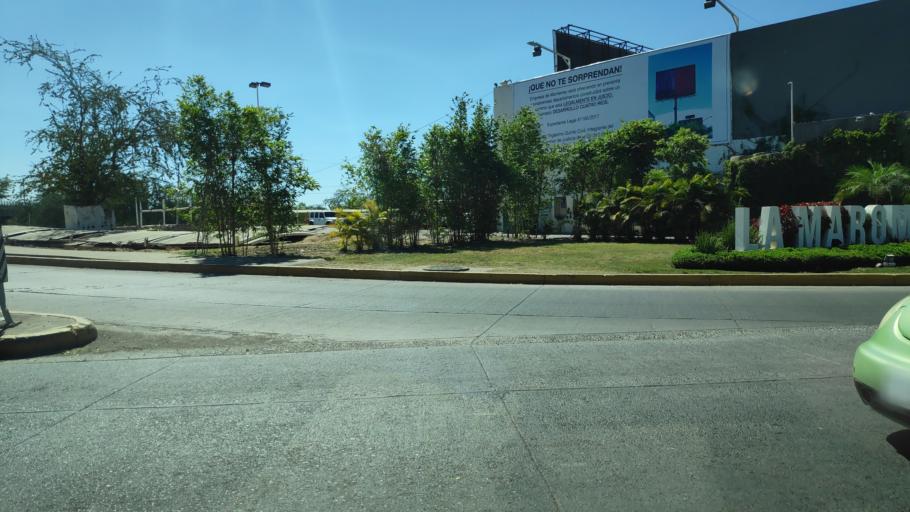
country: MX
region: Sinaloa
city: Culiacan
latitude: 24.8219
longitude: -107.4004
